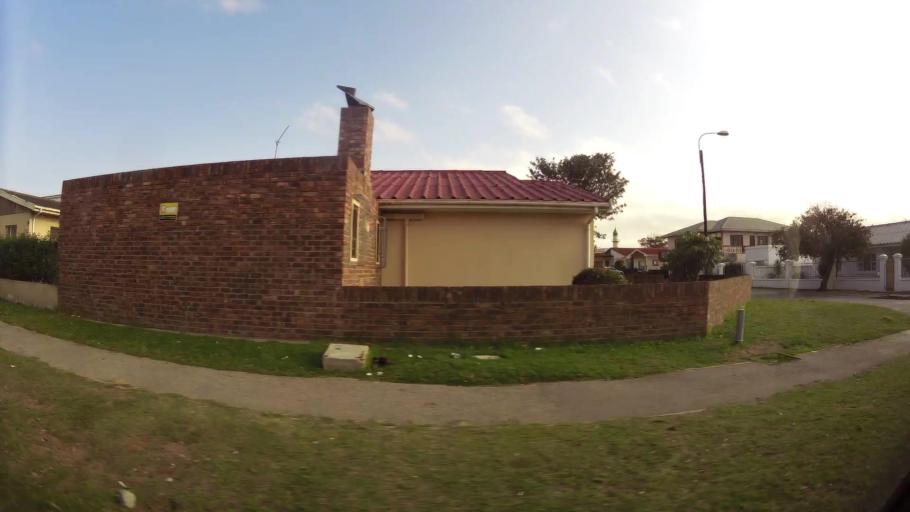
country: ZA
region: Eastern Cape
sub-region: Nelson Mandela Bay Metropolitan Municipality
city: Port Elizabeth
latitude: -33.9209
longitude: 25.5617
